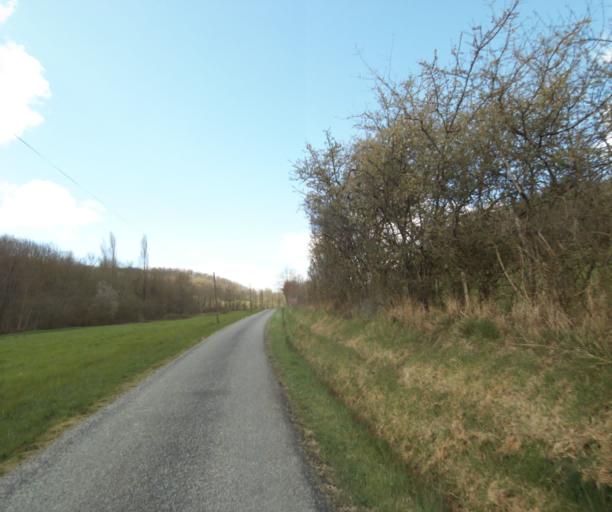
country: FR
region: Midi-Pyrenees
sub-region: Departement de l'Ariege
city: Saverdun
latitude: 43.1848
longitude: 1.5577
